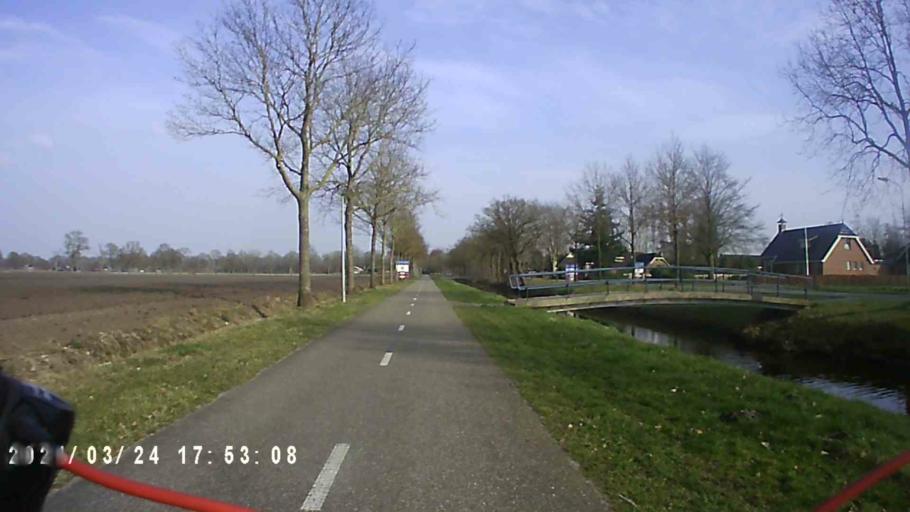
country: NL
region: Groningen
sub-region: Gemeente Leek
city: Leek
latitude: 53.1229
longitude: 6.3554
